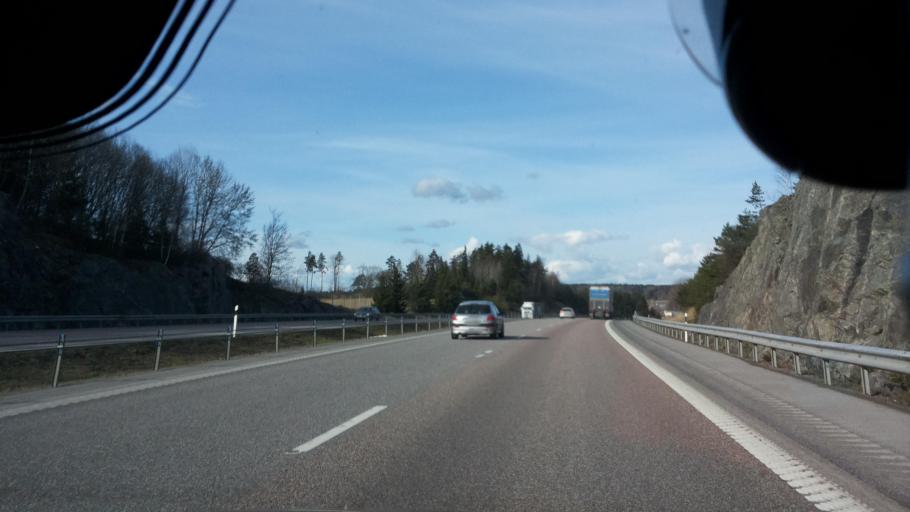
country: SE
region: Soedermanland
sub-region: Trosa Kommun
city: Vagnharad
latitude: 58.9975
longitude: 17.5367
